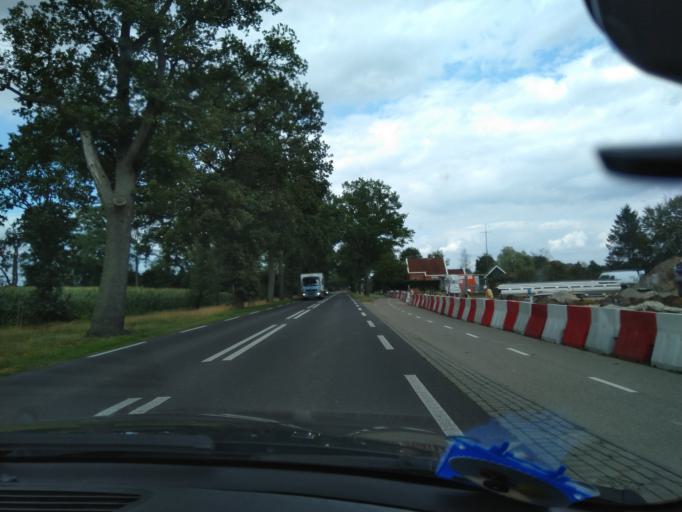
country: NL
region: Groningen
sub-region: Gemeente Groningen
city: Groningen
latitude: 53.1585
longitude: 6.4949
